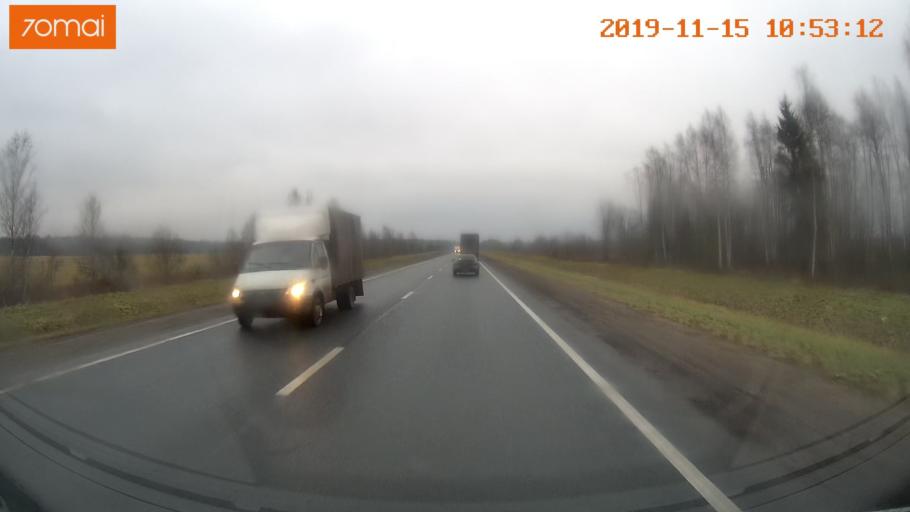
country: RU
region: Vologda
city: Chebsara
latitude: 59.1704
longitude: 38.7491
